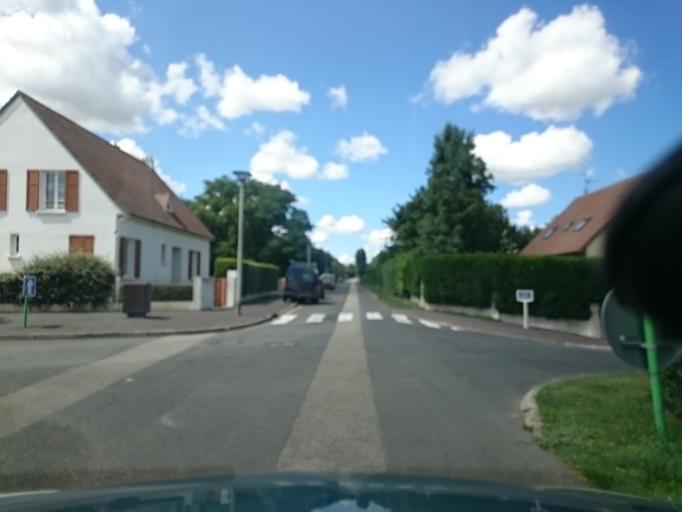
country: FR
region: Lower Normandy
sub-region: Departement du Calvados
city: Ifs
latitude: 49.1453
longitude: -0.3534
